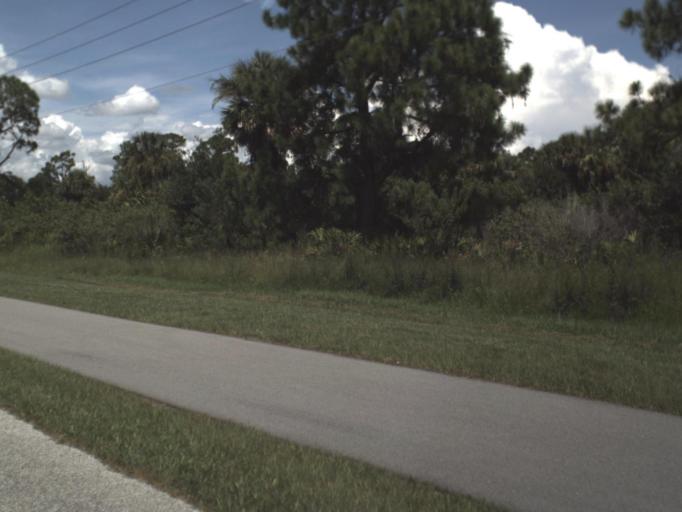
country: US
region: Florida
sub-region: Charlotte County
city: Charlotte Park
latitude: 26.8937
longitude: -82.0258
